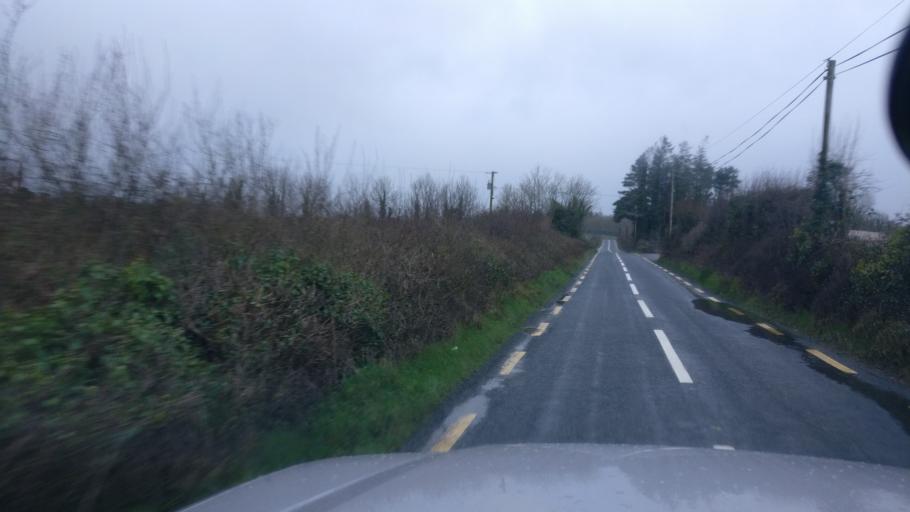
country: IE
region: Connaught
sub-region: County Galway
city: Loughrea
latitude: 53.0998
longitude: -8.4089
